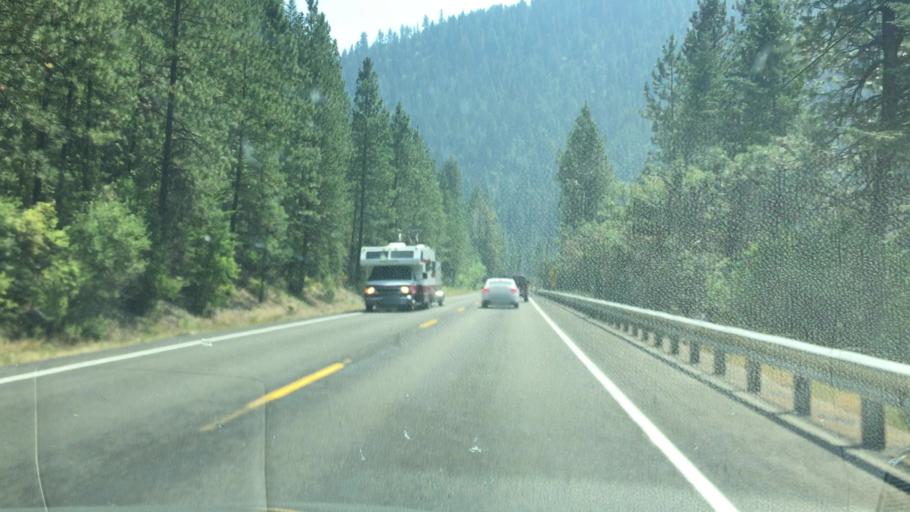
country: US
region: Idaho
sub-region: Valley County
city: McCall
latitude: 45.1529
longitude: -116.2972
